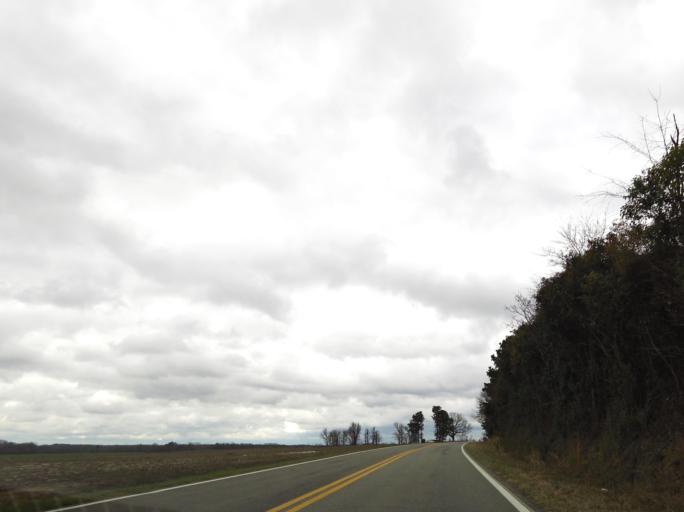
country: US
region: Georgia
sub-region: Twiggs County
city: Jeffersonville
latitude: 32.5834
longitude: -83.3760
